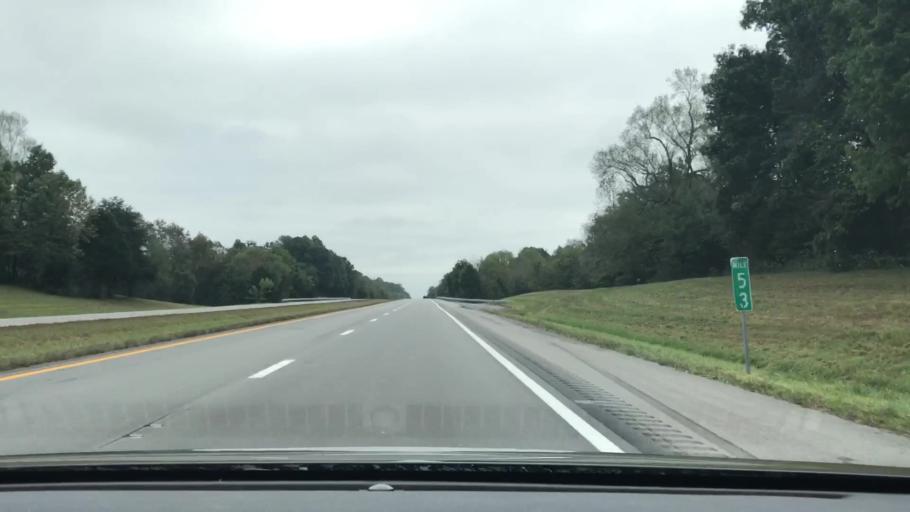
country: US
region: Kentucky
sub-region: Adair County
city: Columbia
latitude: 37.0764
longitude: -85.2322
